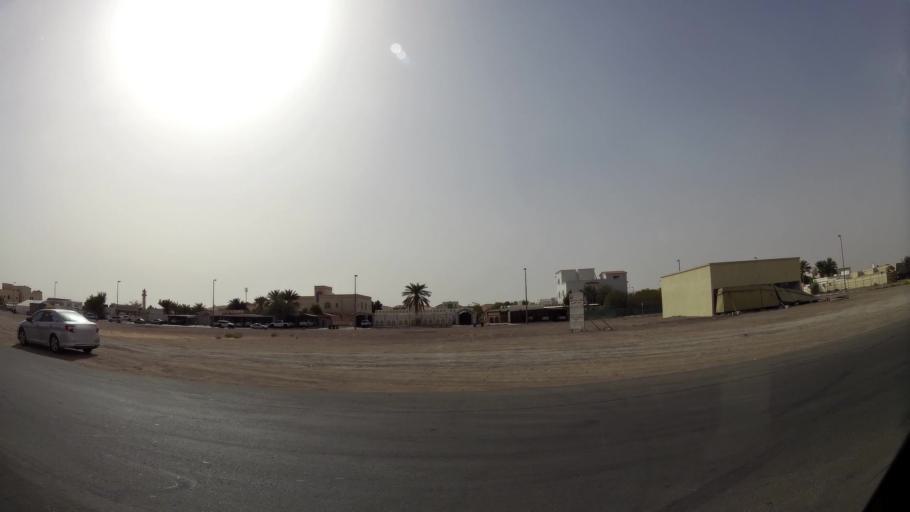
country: AE
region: Abu Dhabi
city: Al Ain
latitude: 24.2102
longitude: 55.5912
